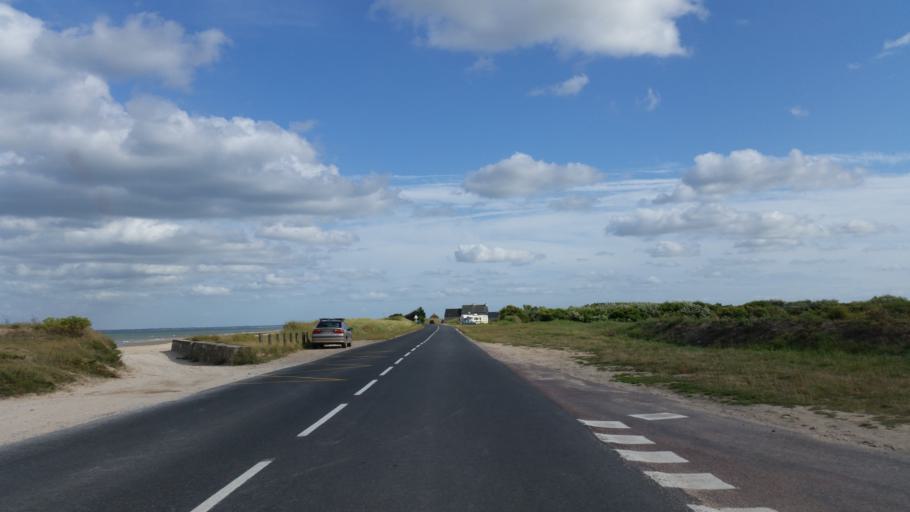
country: FR
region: Lower Normandy
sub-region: Departement de la Manche
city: Sainte-Mere-Eglise
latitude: 49.4532
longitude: -1.2200
